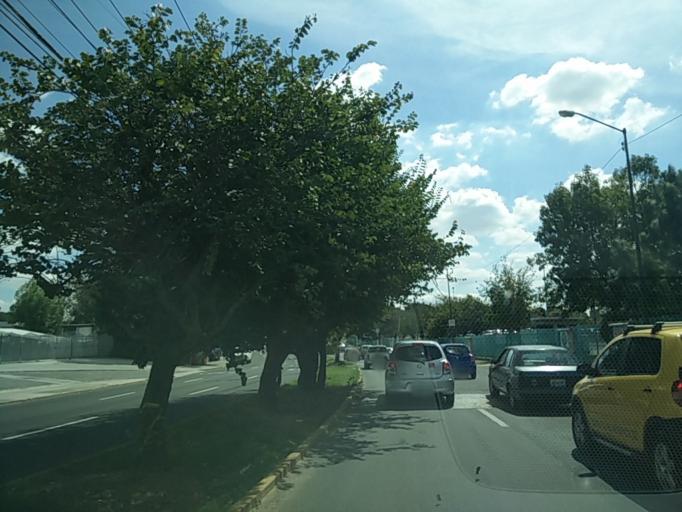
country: MX
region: Jalisco
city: Zapopan2
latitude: 20.7262
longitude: -103.4311
